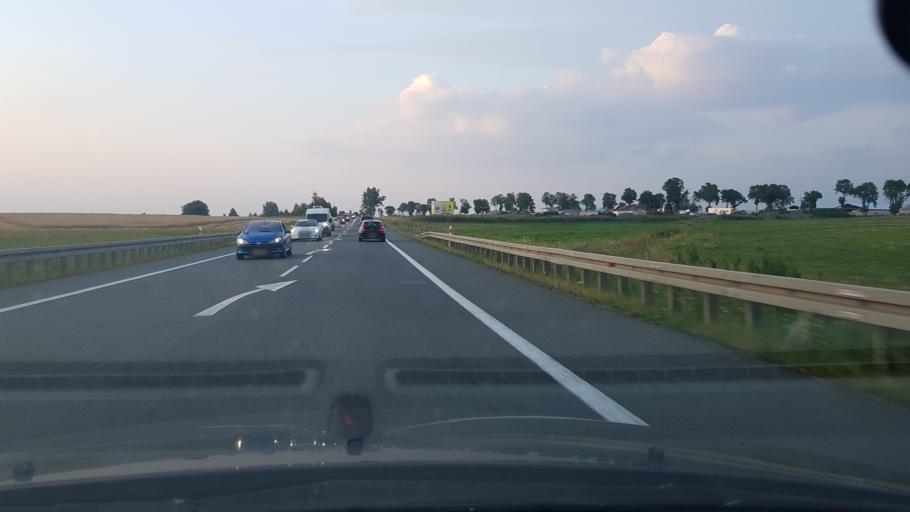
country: PL
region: Masovian Voivodeship
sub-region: Powiat mlawski
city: Wieczfnia Koscielna
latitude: 53.1921
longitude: 20.4337
